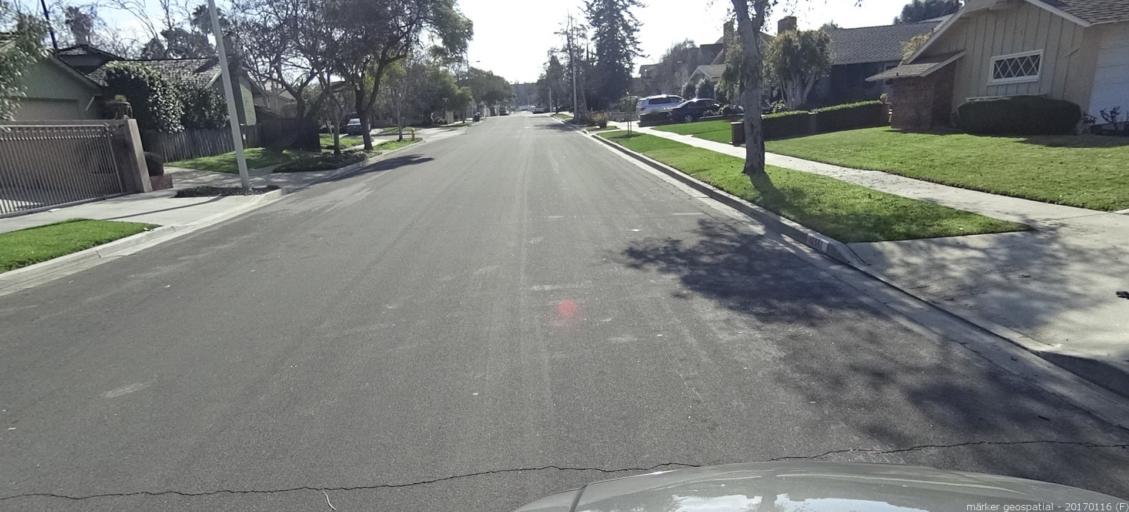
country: US
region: California
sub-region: Orange County
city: Rossmoor
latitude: 33.7804
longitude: -118.0795
